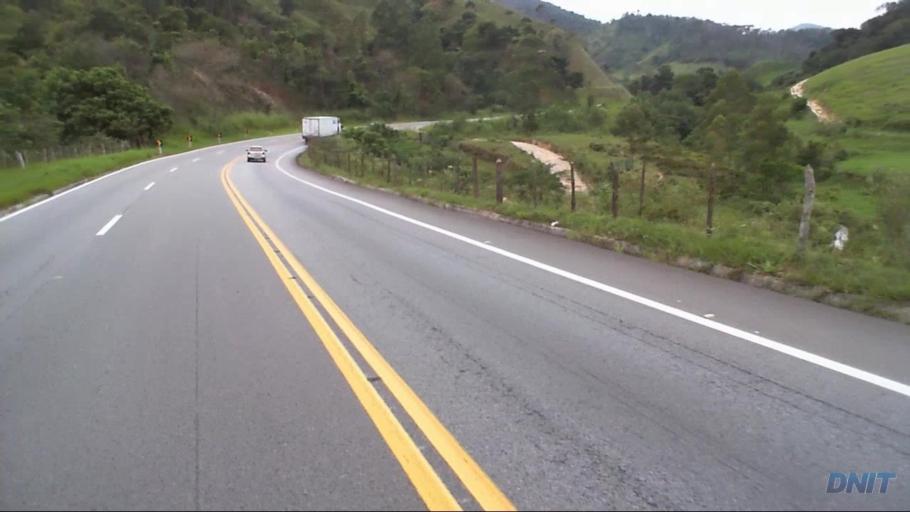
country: BR
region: Minas Gerais
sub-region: Nova Era
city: Nova Era
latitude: -19.6292
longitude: -42.8735
